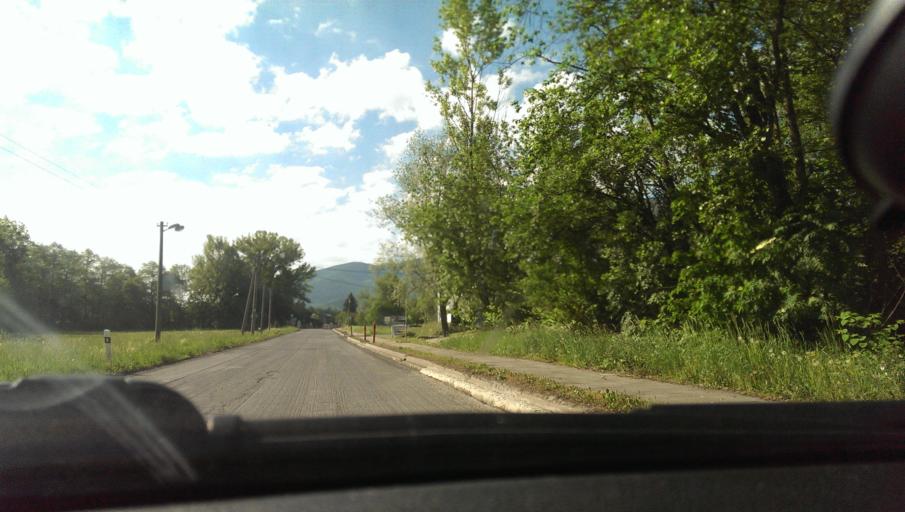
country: CZ
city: Frydlant nad Ostravici
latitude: 49.5753
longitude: 18.3588
